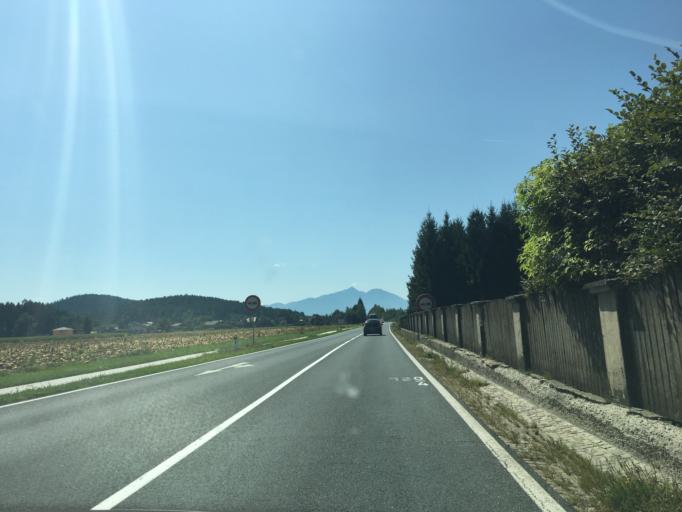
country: AT
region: Carinthia
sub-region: Politischer Bezirk Volkermarkt
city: Voelkermarkt
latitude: 46.6768
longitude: 14.6717
